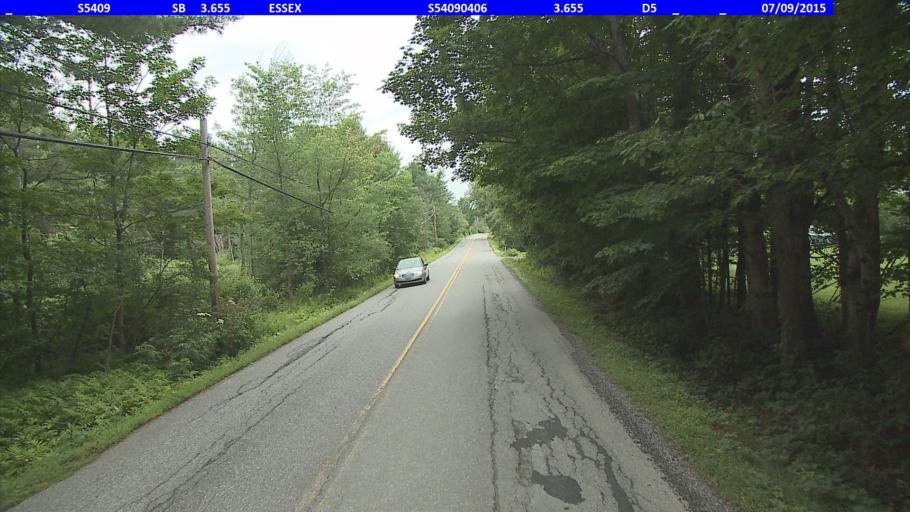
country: US
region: Vermont
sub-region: Chittenden County
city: Essex Junction
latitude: 44.5601
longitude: -73.0644
